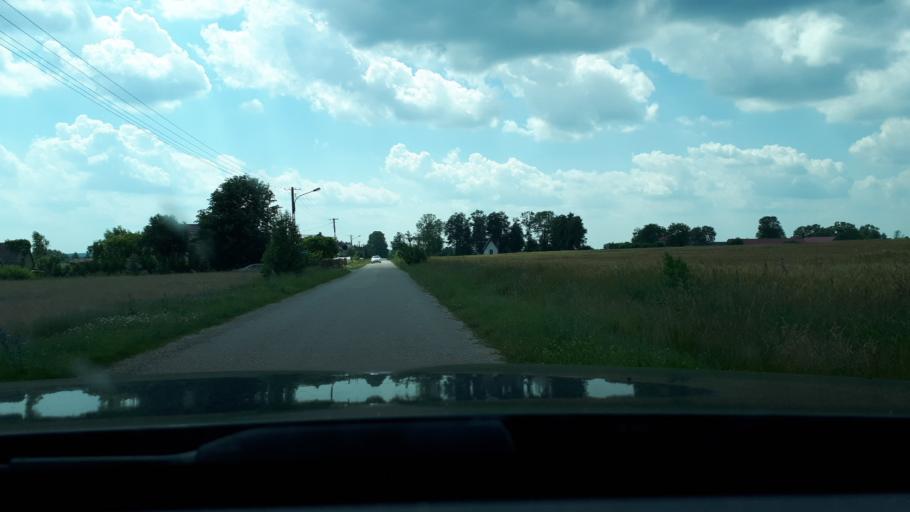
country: PL
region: Podlasie
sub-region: Powiat bialostocki
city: Lapy
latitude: 53.0875
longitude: 22.8382
